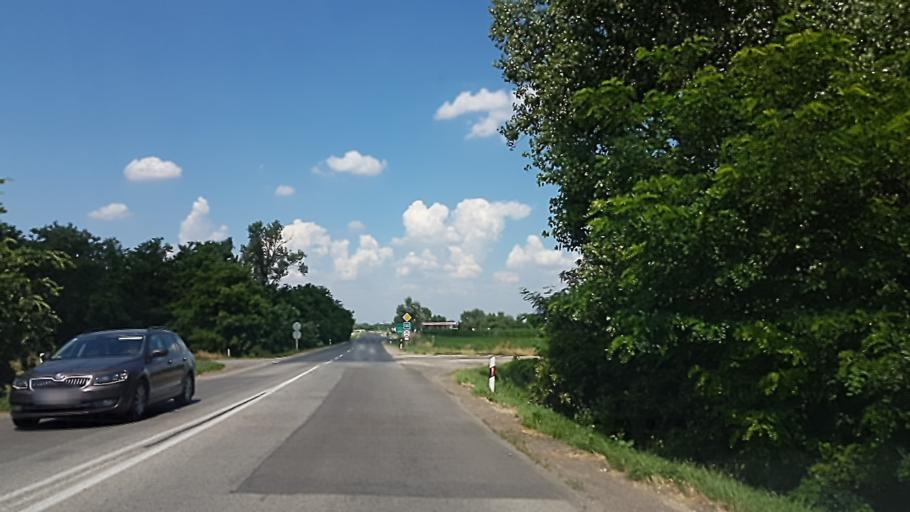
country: HU
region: Komarom-Esztergom
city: Nagyigmand
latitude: 47.6758
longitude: 18.0923
